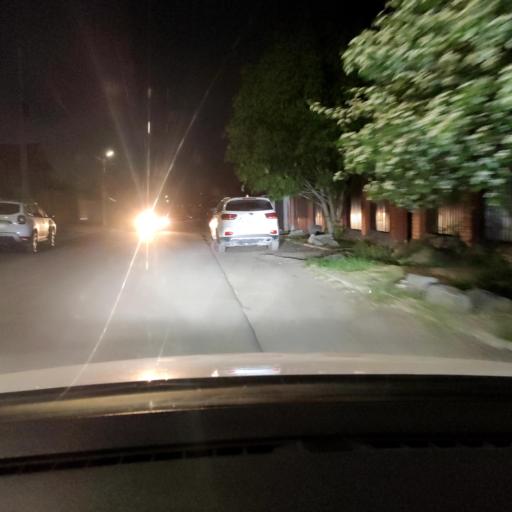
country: RU
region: Voronezj
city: Pridonskoy
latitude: 51.6586
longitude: 39.0598
